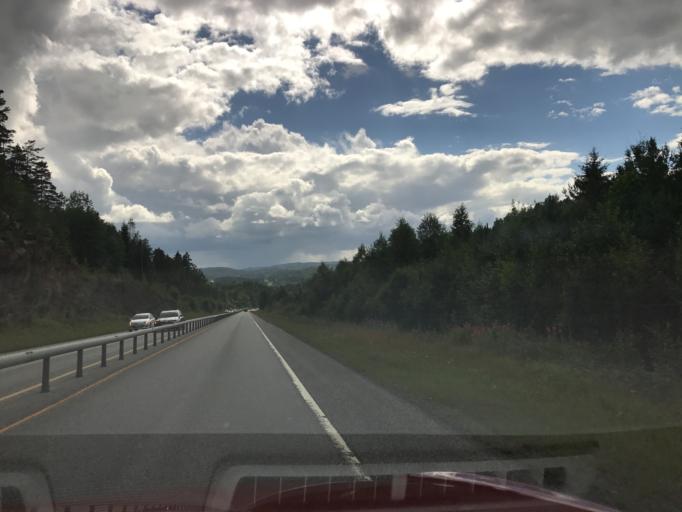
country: NO
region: Aust-Agder
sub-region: Gjerstad
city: Gjerstad
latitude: 58.8558
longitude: 9.1298
